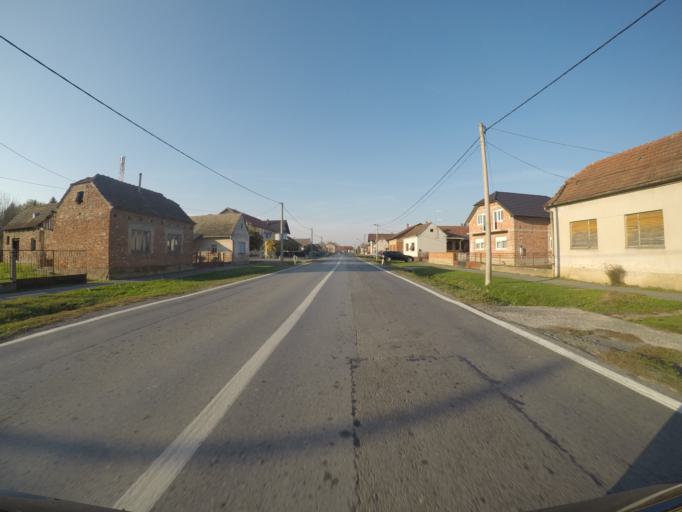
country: HU
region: Somogy
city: Barcs
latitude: 45.9058
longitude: 17.4417
